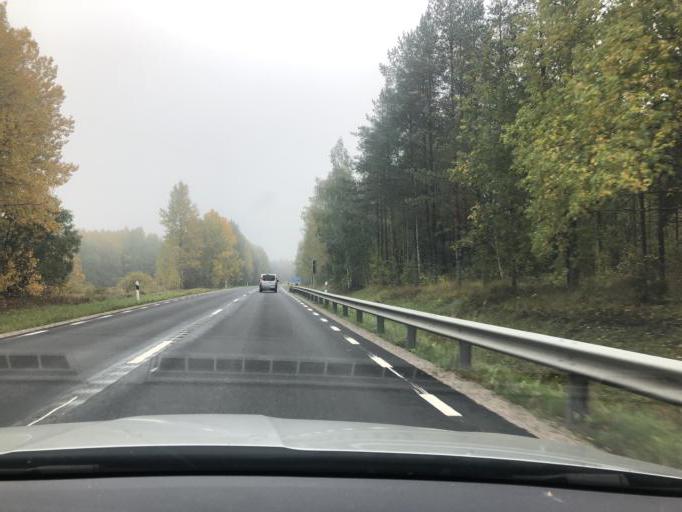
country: SE
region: Uppsala
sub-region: Tierps Kommun
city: Orbyhus
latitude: 60.2594
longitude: 17.6255
